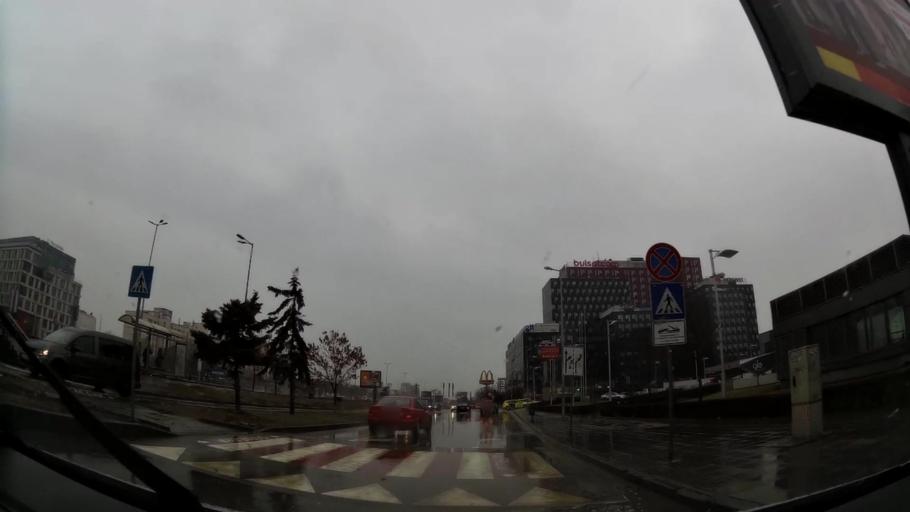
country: BG
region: Sofia-Capital
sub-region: Stolichna Obshtina
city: Sofia
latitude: 42.6600
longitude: 23.3812
